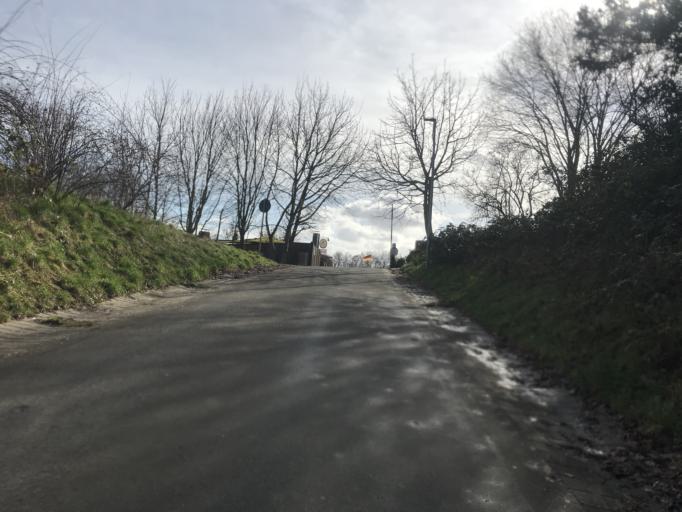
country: DE
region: Hesse
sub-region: Regierungsbezirk Darmstadt
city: Hochheim am Main
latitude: 50.0601
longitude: 8.3749
